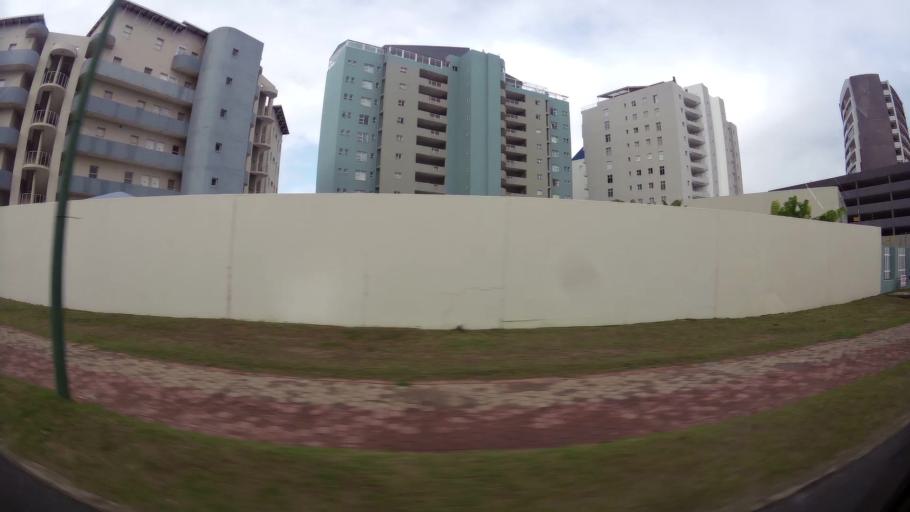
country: ZA
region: Western Cape
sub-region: Eden District Municipality
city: Mossel Bay
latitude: -34.1577
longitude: 22.1086
